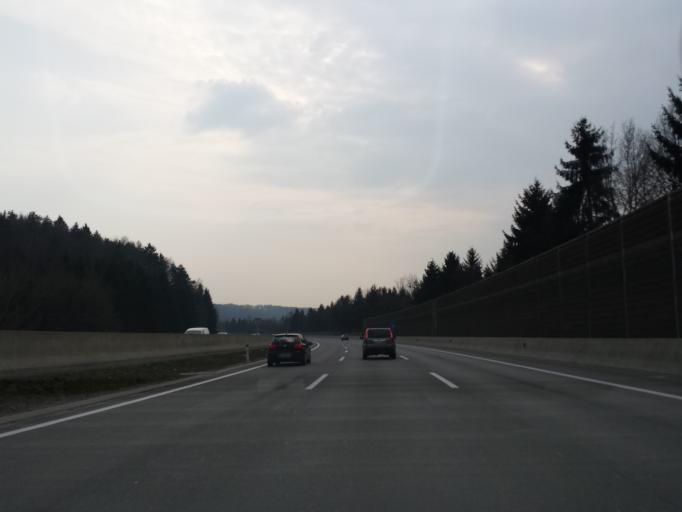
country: AT
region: Styria
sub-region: Politischer Bezirk Graz-Umgebung
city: Hart bei Graz
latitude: 47.0547
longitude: 15.5380
